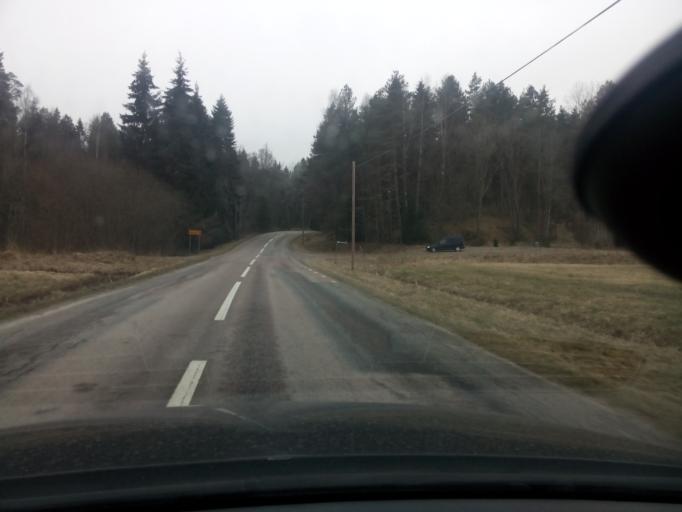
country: SE
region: Soedermanland
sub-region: Gnesta Kommun
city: Gnesta
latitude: 58.9931
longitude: 17.1663
